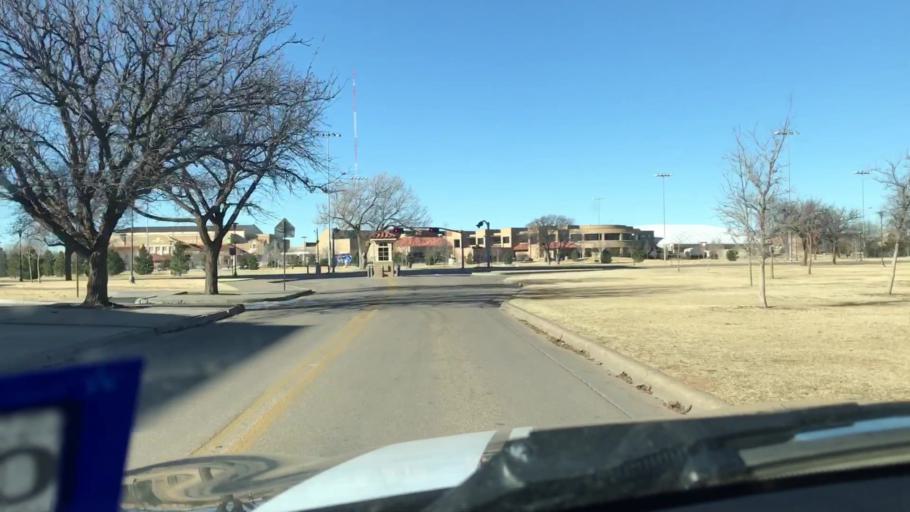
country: US
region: Texas
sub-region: Lubbock County
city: Lubbock
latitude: 33.5827
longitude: -101.8805
